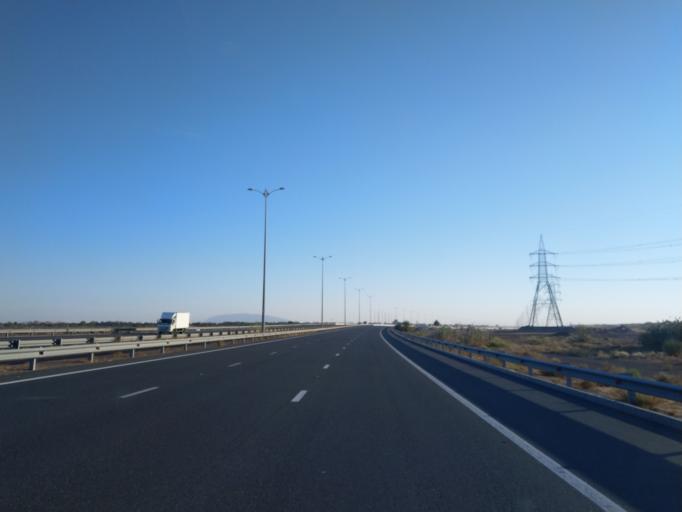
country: OM
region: Al Buraimi
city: Al Buraymi
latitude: 24.3771
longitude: 55.7975
